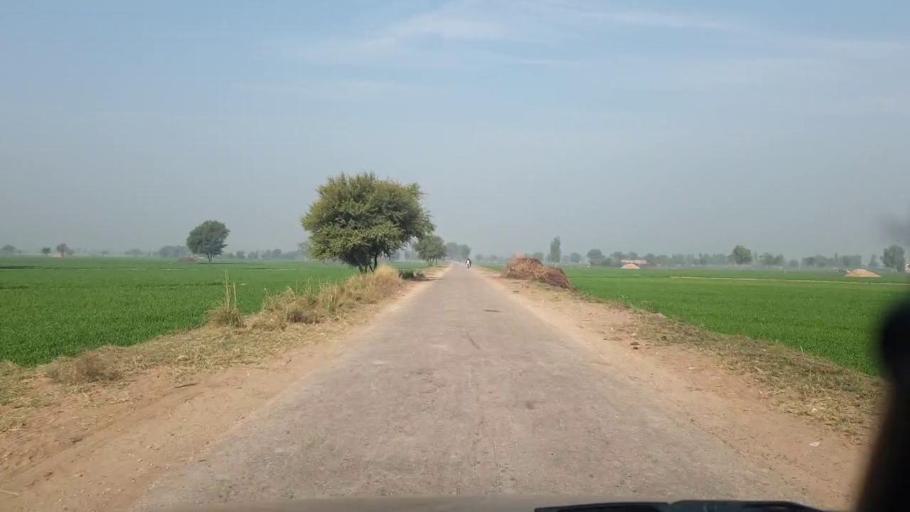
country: PK
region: Sindh
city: Shahdadpur
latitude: 26.0037
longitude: 68.5534
